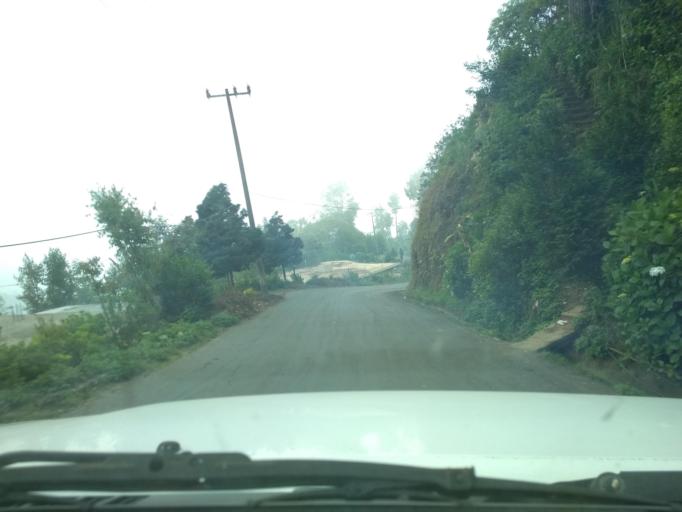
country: MX
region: Veracruz
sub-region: La Perla
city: Chilapa
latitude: 18.9646
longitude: -97.1678
